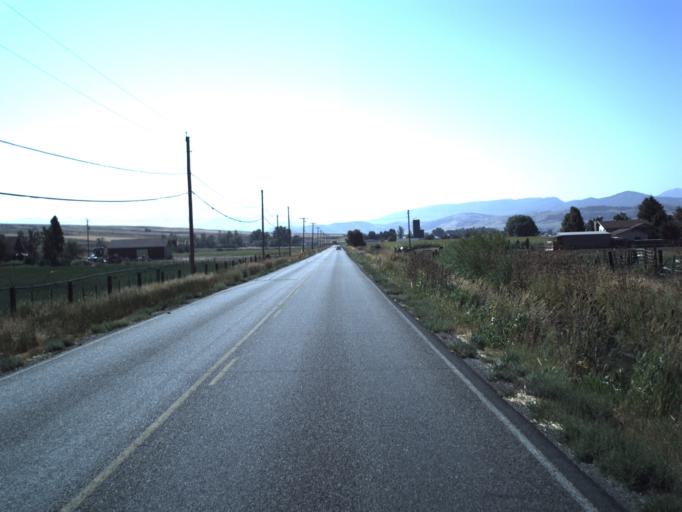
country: US
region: Utah
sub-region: Cache County
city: Hyrum
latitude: 41.6148
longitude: -111.8328
